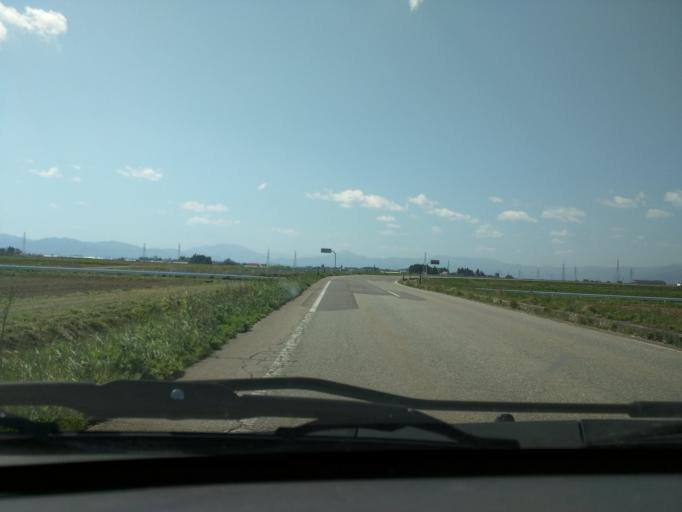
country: JP
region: Fukushima
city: Kitakata
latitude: 37.5841
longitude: 139.8699
